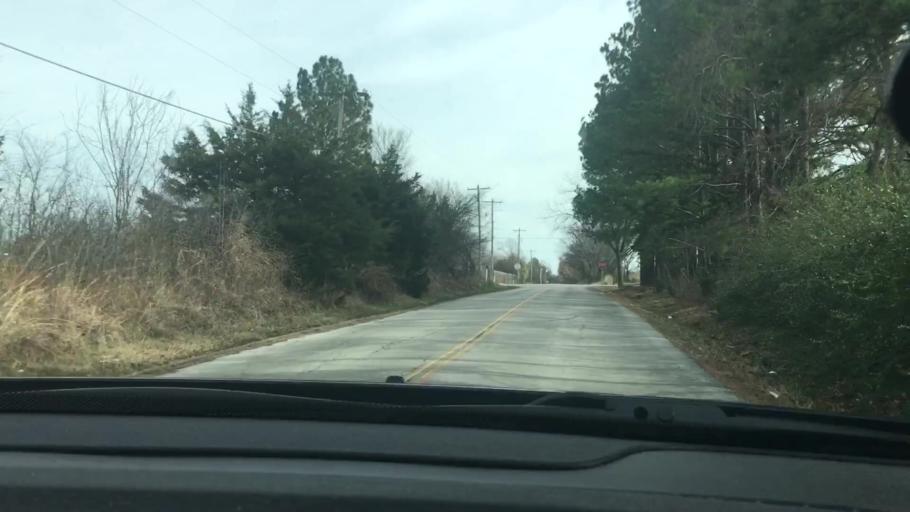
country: US
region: Oklahoma
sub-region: Carter County
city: Ardmore
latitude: 34.1727
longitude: -97.0742
